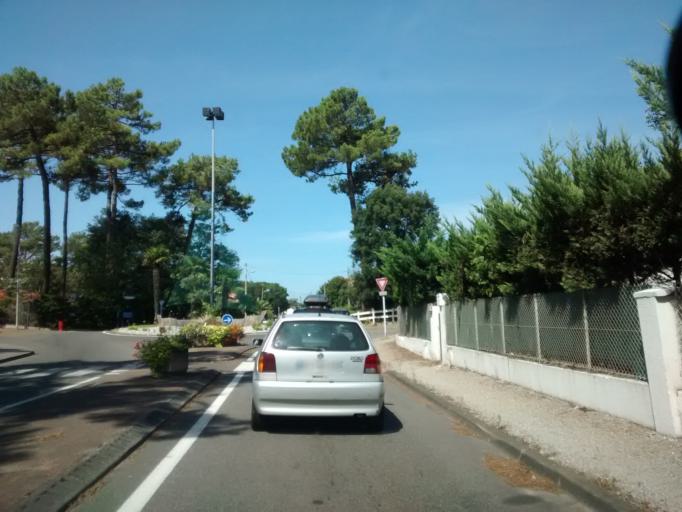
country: FR
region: Aquitaine
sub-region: Departement des Landes
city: Capbreton
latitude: 43.6367
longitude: -1.4211
